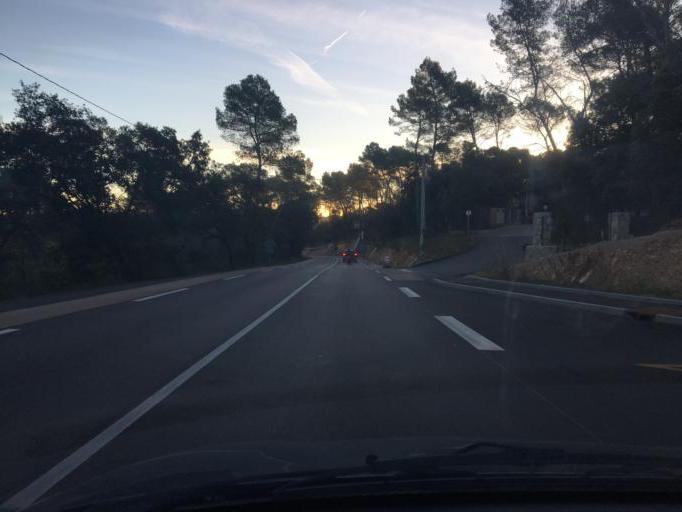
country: FR
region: Provence-Alpes-Cote d'Azur
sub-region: Departement du Var
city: Taradeau
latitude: 43.4606
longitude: 6.4092
